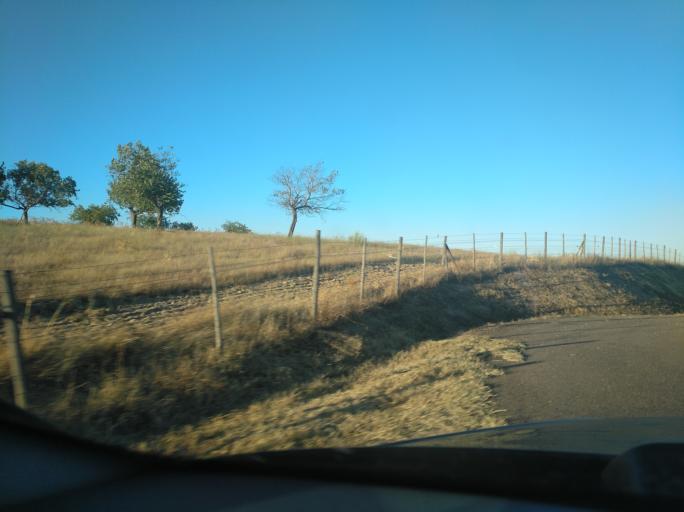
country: PT
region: Portalegre
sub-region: Arronches
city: Arronches
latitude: 39.0675
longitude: -7.2206
